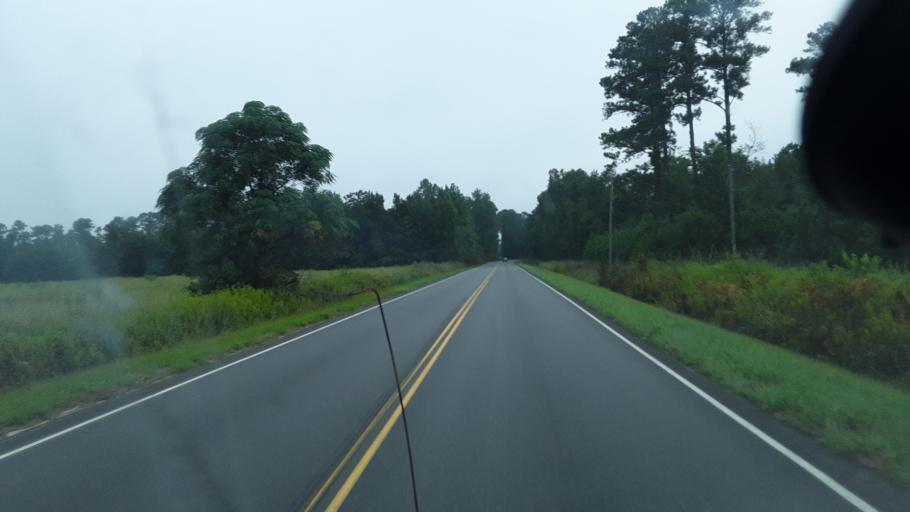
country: US
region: South Carolina
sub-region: Florence County
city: Johnsonville
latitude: 33.8898
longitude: -79.4483
